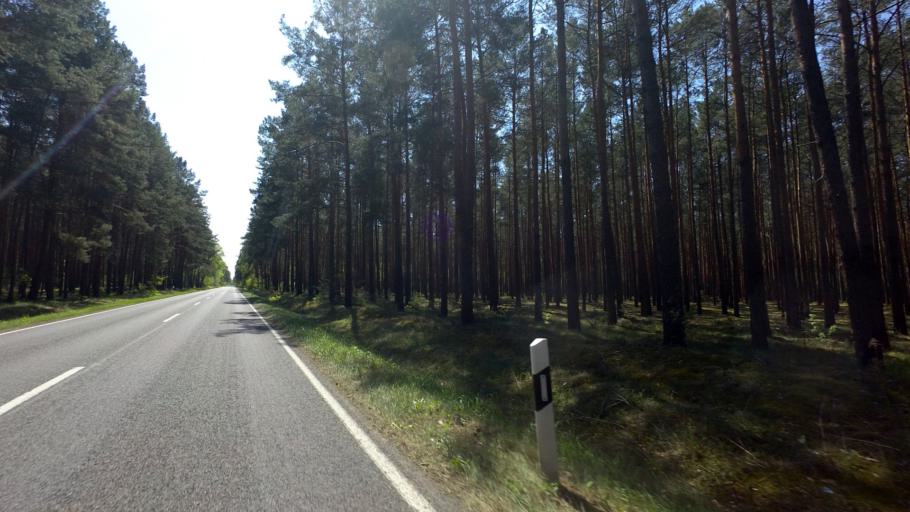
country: DE
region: Brandenburg
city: Gross Koris
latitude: 52.2063
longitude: 13.6912
